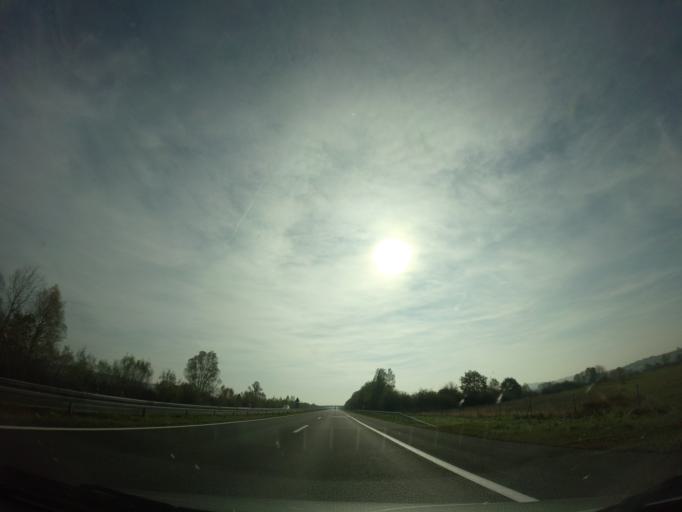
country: HR
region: Zagrebacka
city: Brckovljani
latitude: 45.9771
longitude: 16.2848
